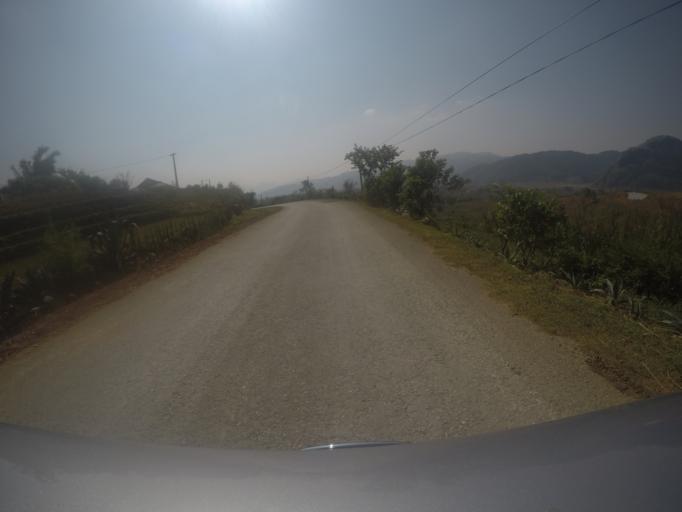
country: VN
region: Lai Chau
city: Than Uyen
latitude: 22.0255
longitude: 103.9335
